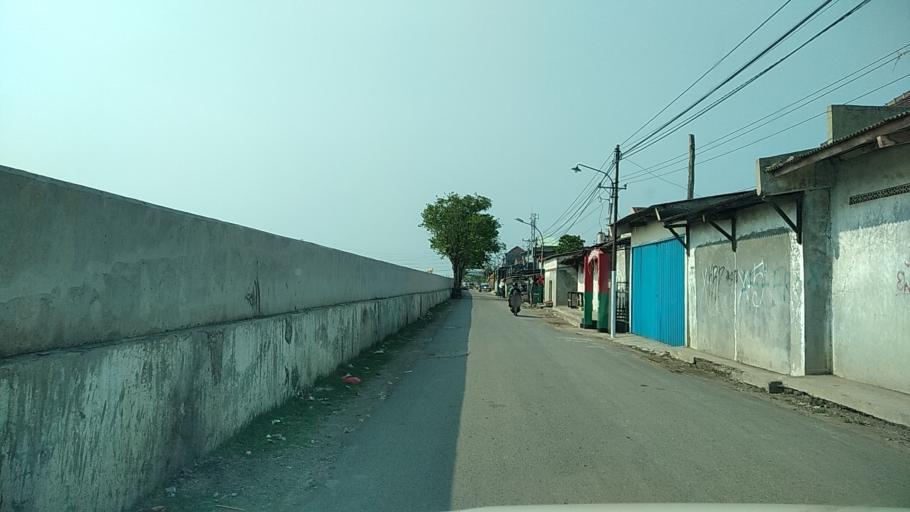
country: ID
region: Central Java
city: Semarang
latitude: -6.9589
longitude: 110.4425
